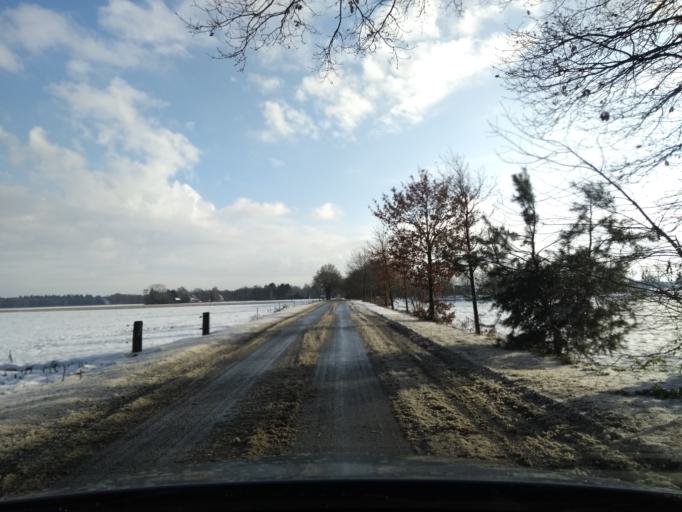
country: NL
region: Gelderland
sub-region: Gemeente Bronckhorst
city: Zelhem
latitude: 52.0342
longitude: 6.3442
